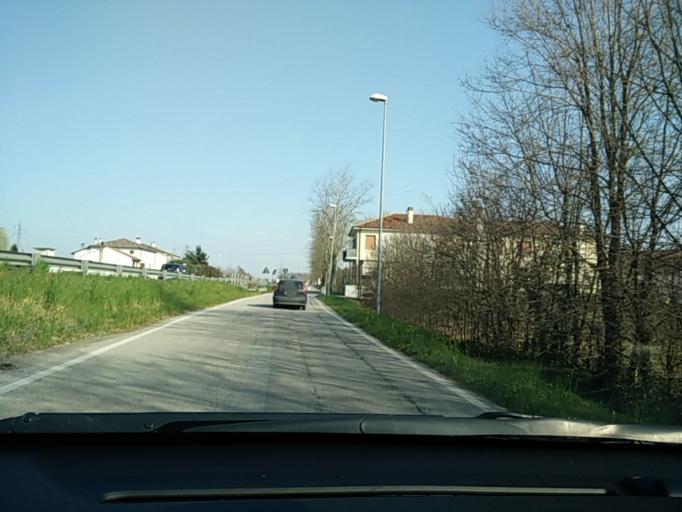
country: IT
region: Veneto
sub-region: Provincia di Treviso
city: Monastier di Treviso
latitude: 45.6362
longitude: 12.4151
